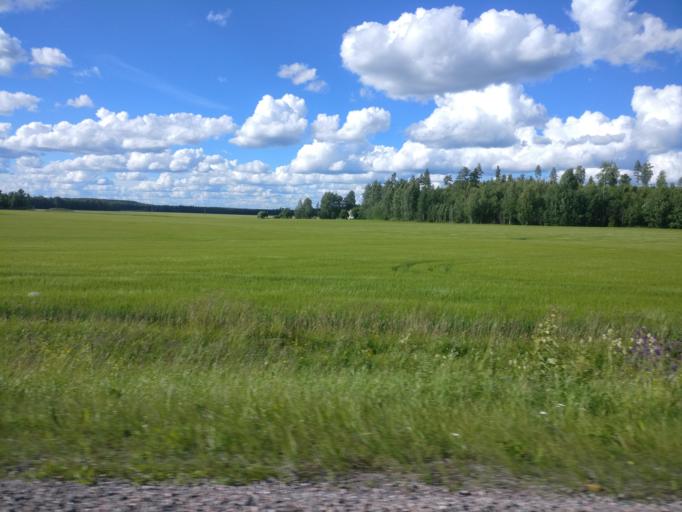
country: FI
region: Uusimaa
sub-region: Helsinki
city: Hyvinge
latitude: 60.6181
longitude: 24.9693
